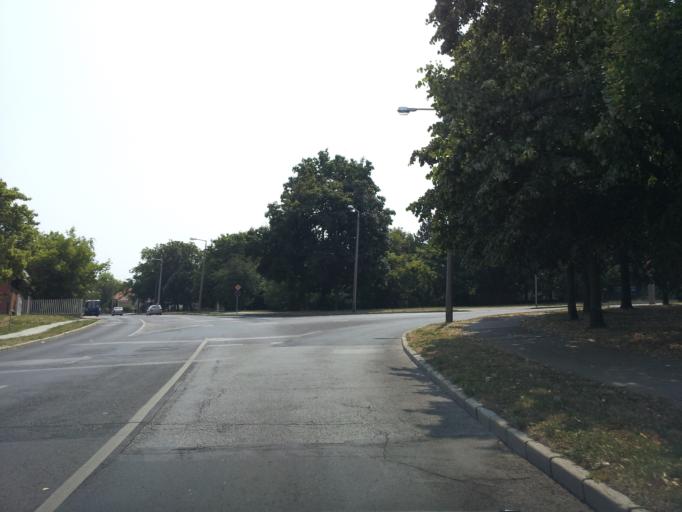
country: HU
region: Veszprem
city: Veszprem
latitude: 47.1048
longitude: 17.9192
